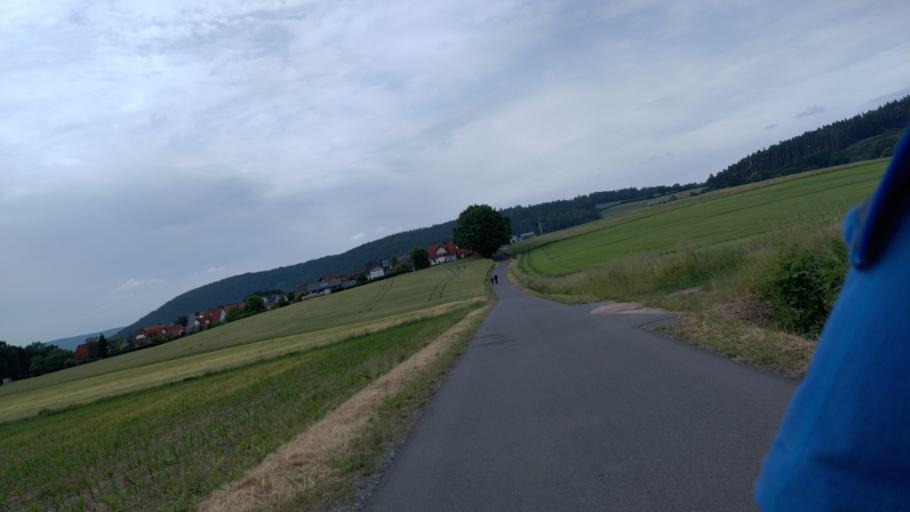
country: DE
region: Bavaria
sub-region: Upper Franconia
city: Harsdorf
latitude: 50.0212
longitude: 11.5756
